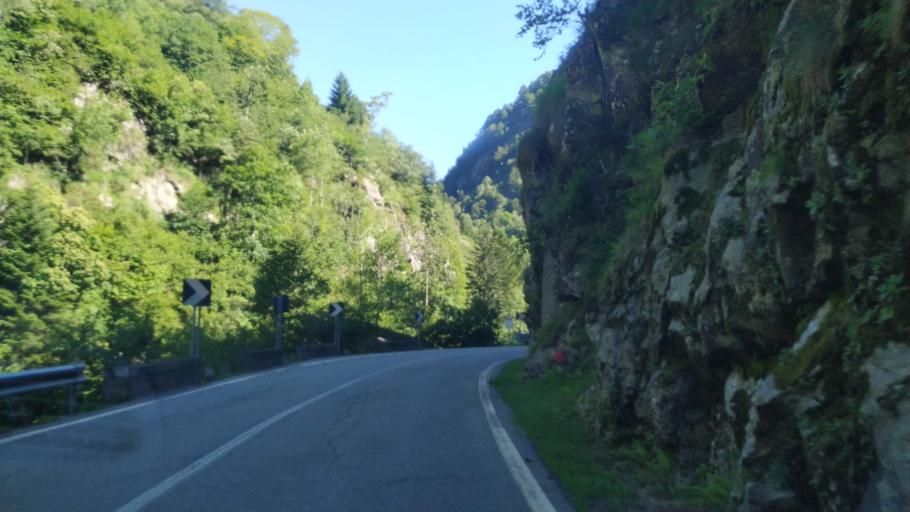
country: IT
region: Piedmont
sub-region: Provincia di Vercelli
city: Rimasco
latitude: 45.8459
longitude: 8.0659
